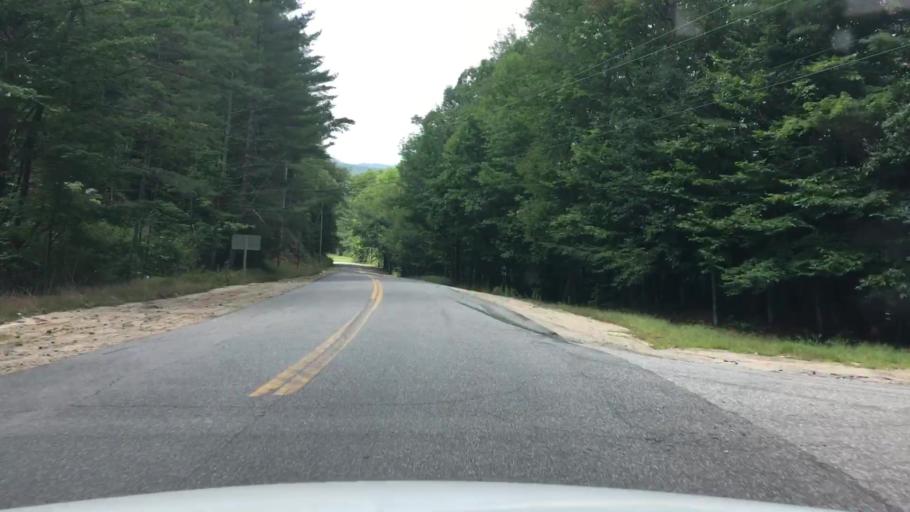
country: US
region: Maine
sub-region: Oxford County
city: Rumford
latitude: 44.5476
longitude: -70.6823
